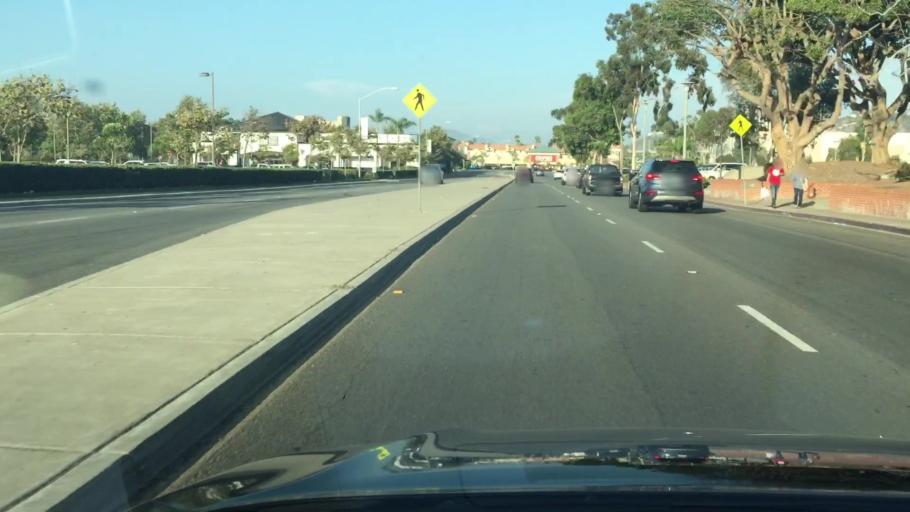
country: US
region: California
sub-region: San Diego County
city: San Diego
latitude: 32.7701
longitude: -117.1493
